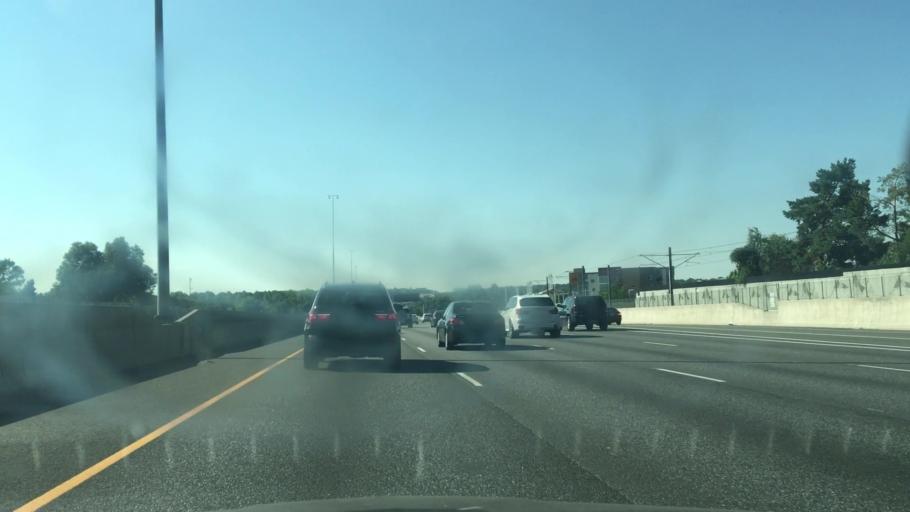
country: US
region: Colorado
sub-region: Arapahoe County
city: Glendale
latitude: 39.6700
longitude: -104.9287
